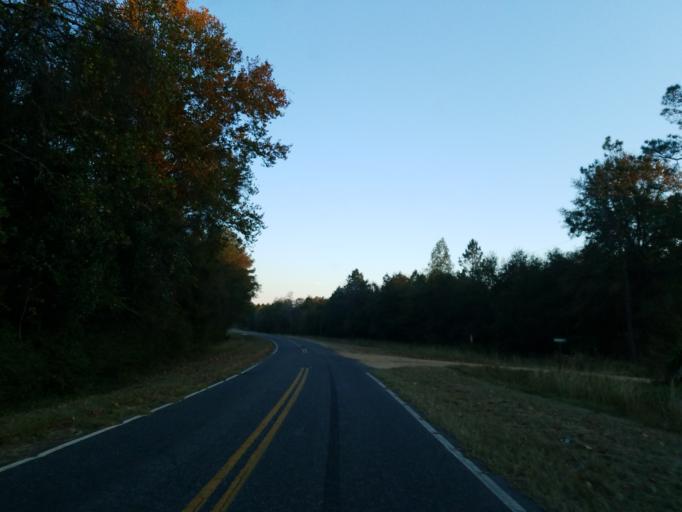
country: US
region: Georgia
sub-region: Ben Hill County
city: Fitzgerald
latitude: 31.6566
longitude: -83.3904
